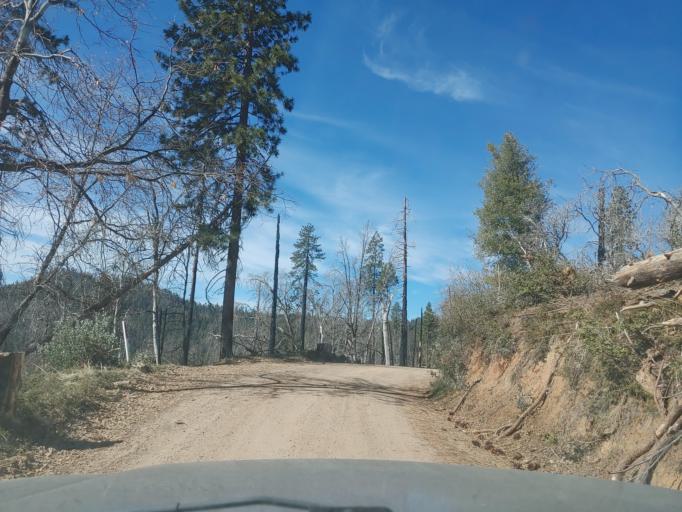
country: US
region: California
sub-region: Madera County
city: Ahwahnee
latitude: 37.4361
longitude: -119.6593
